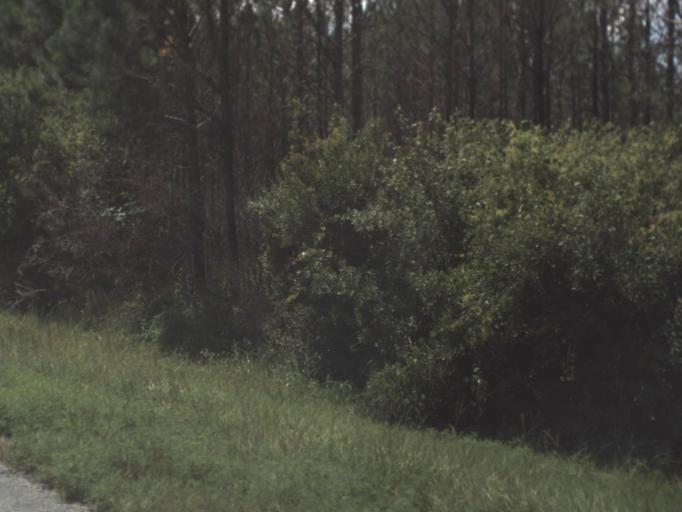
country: US
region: Florida
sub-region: Columbia County
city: Five Points
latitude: 30.5686
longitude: -82.4381
